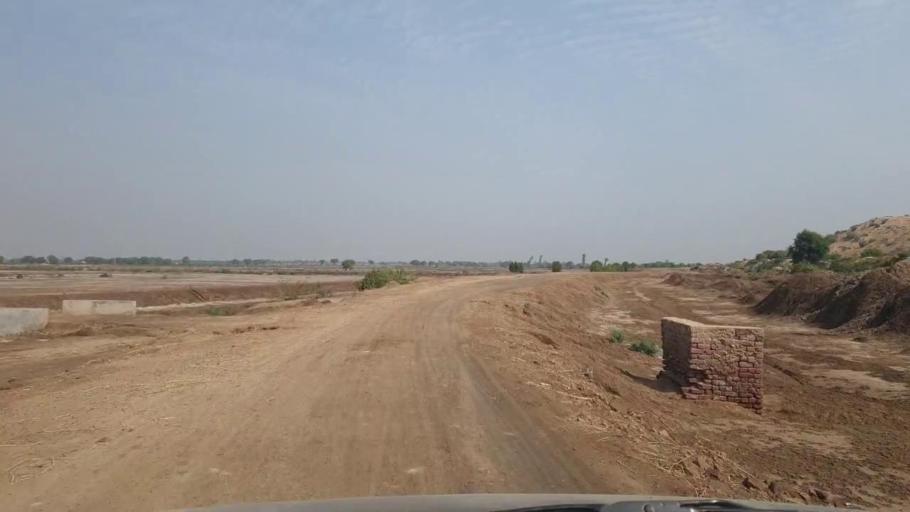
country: PK
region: Sindh
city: Tando Muhammad Khan
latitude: 25.1485
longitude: 68.4595
